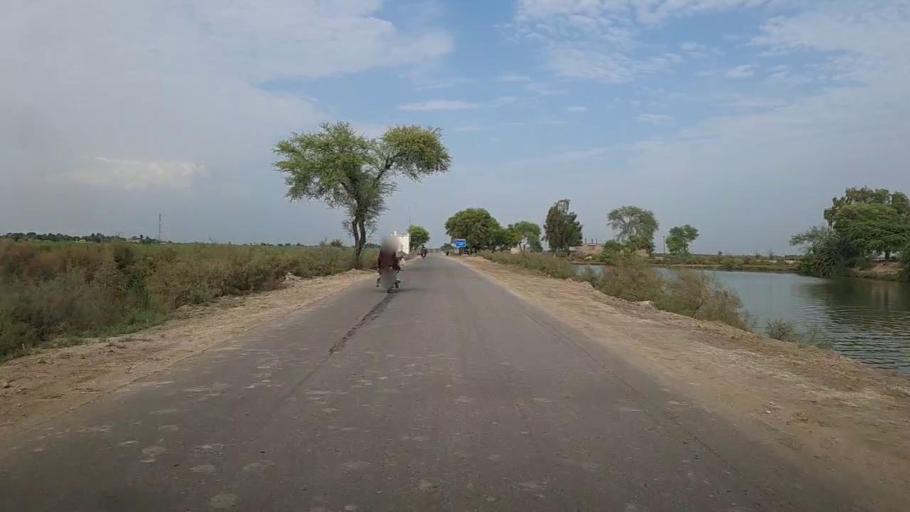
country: PK
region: Sindh
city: Thul
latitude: 28.2808
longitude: 68.8541
